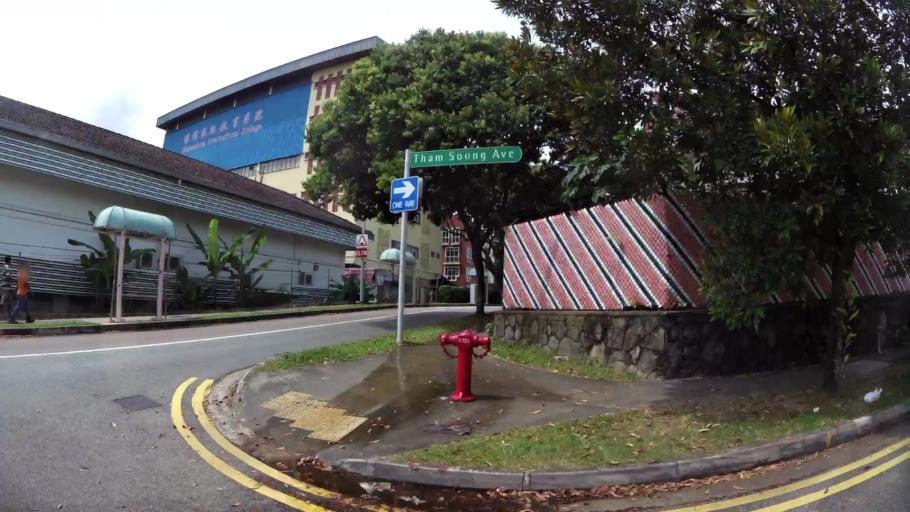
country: SG
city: Singapore
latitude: 1.3419
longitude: 103.7743
